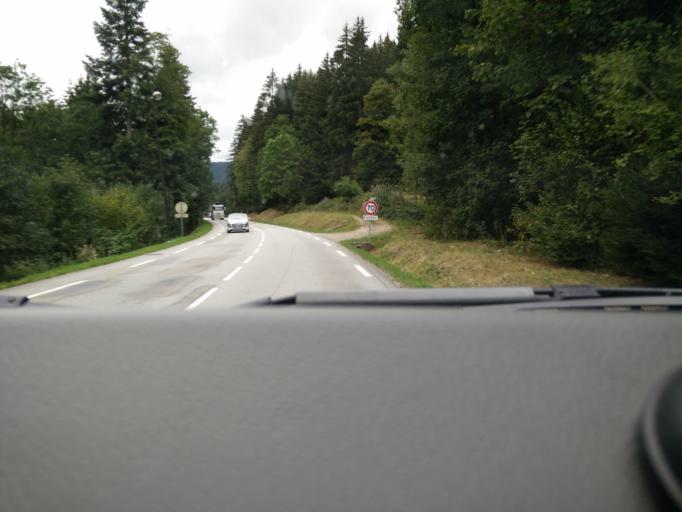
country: FR
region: Lorraine
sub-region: Departement des Vosges
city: Xonrupt-Longemer
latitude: 48.0839
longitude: 6.9169
